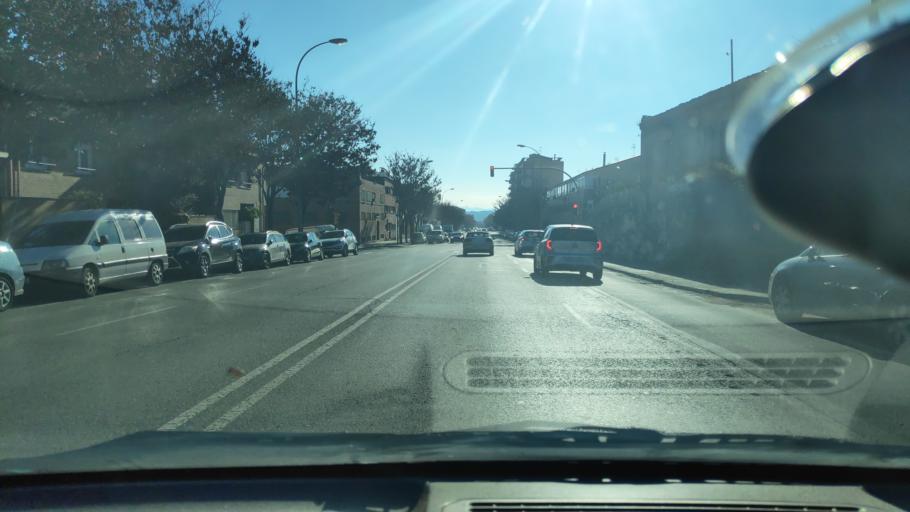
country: ES
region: Catalonia
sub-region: Provincia de Barcelona
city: Sabadell
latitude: 41.5489
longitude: 2.0948
